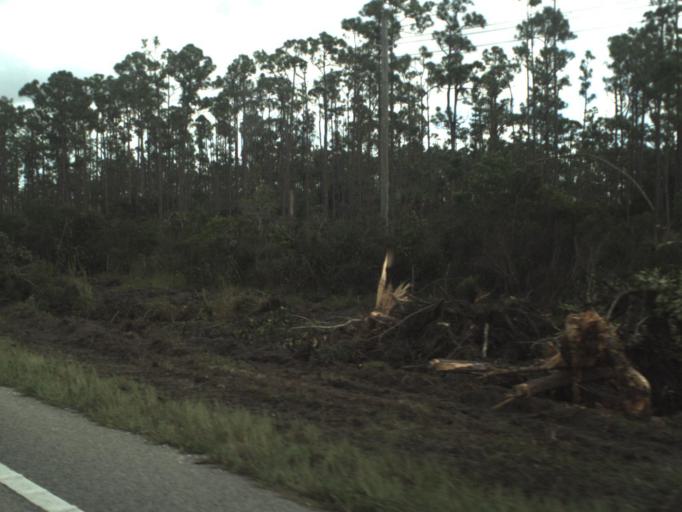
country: US
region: Florida
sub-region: Palm Beach County
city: Limestone Creek
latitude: 26.9064
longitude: -80.2966
